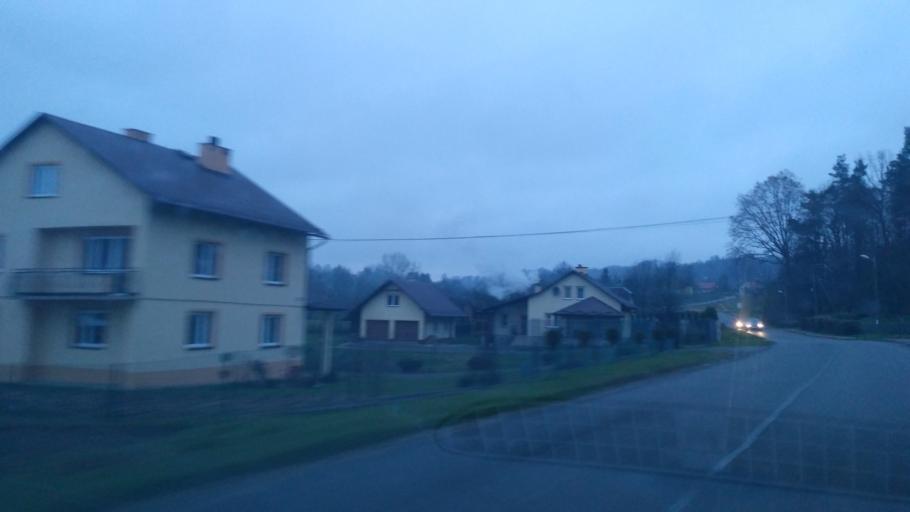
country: PL
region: Subcarpathian Voivodeship
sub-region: Powiat przemyski
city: Nienadowa
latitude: 49.8384
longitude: 22.4335
